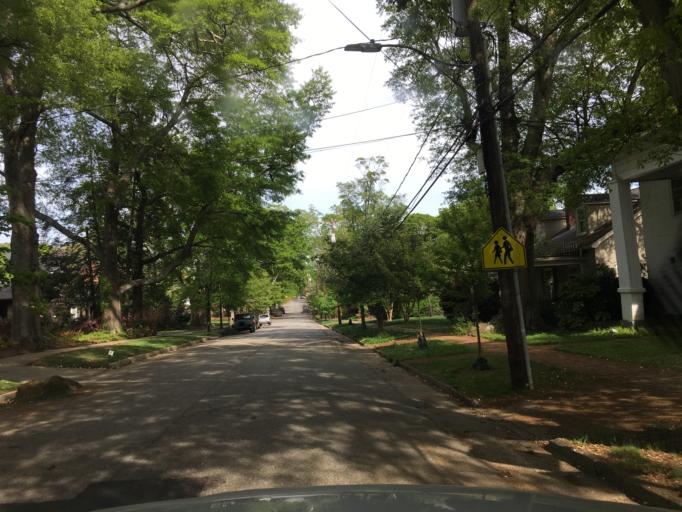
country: US
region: South Carolina
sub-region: Greenville County
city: Greenville
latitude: 34.8633
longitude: -82.3996
